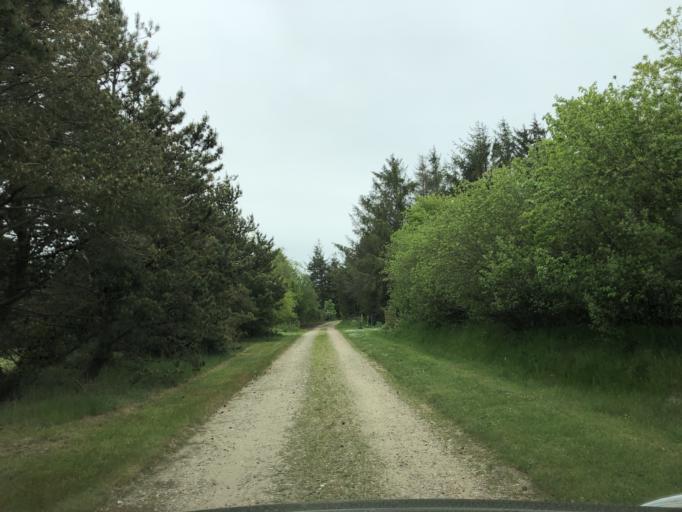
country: DK
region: Central Jutland
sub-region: Holstebro Kommune
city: Ulfborg
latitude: 56.2734
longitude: 8.1646
